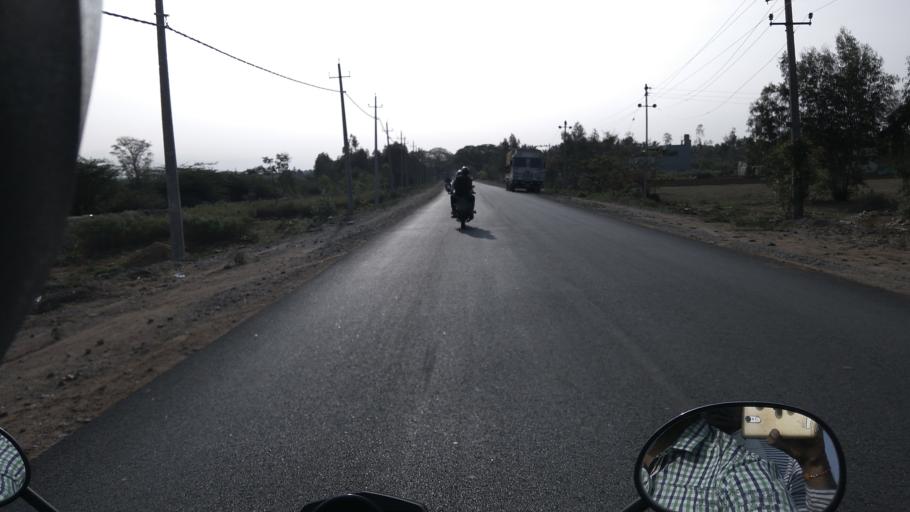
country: IN
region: Karnataka
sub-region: Kolar
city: Kolar
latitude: 13.1159
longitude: 78.1817
